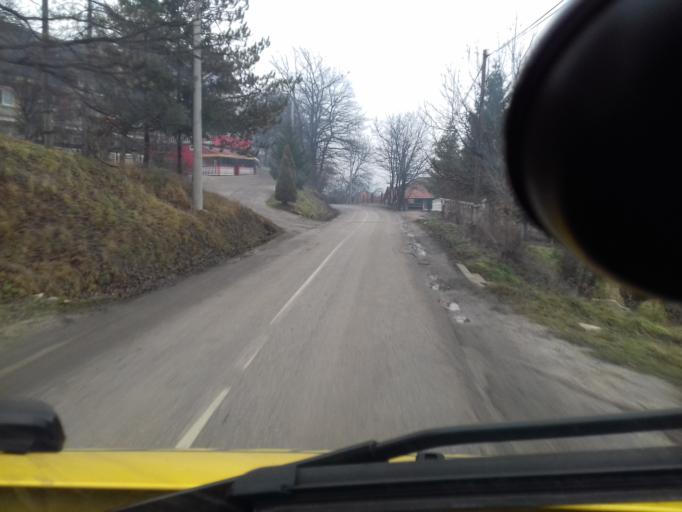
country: BA
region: Federation of Bosnia and Herzegovina
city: Lokvine
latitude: 44.2042
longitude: 17.8590
